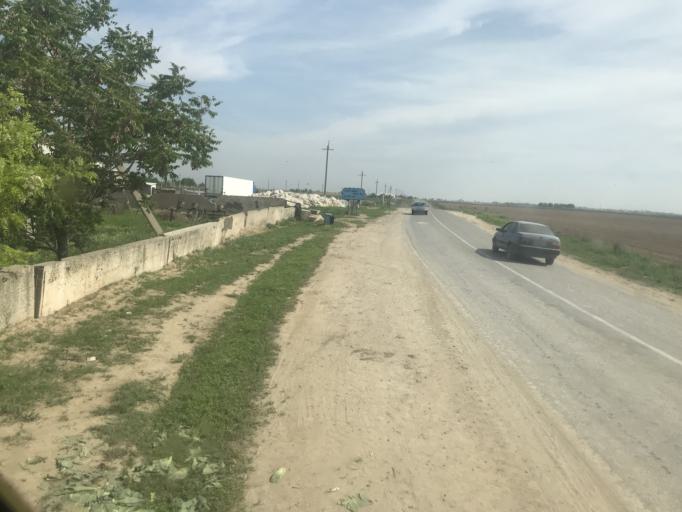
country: UZ
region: Jizzax
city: Gagarin
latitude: 40.9042
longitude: 68.0941
